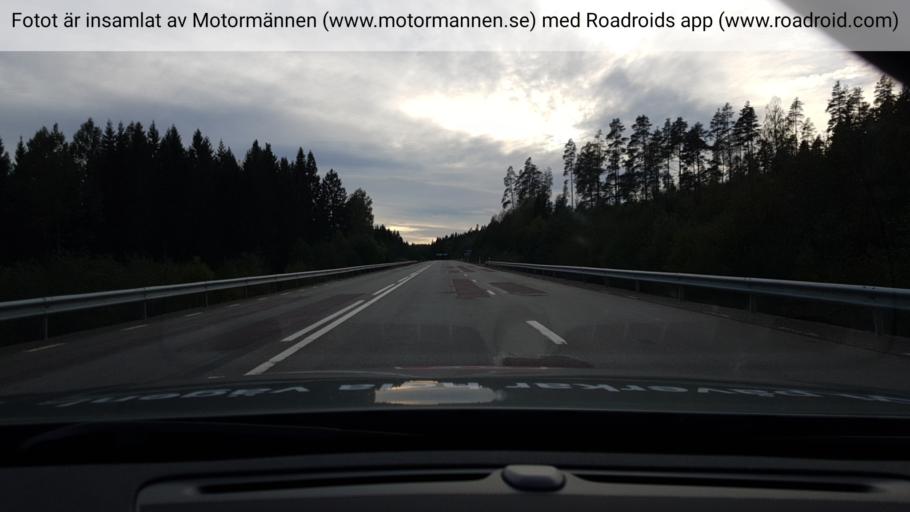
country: SE
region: Vaermland
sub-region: Arjangs Kommun
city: Arjaeng
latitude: 59.3976
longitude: 12.1229
